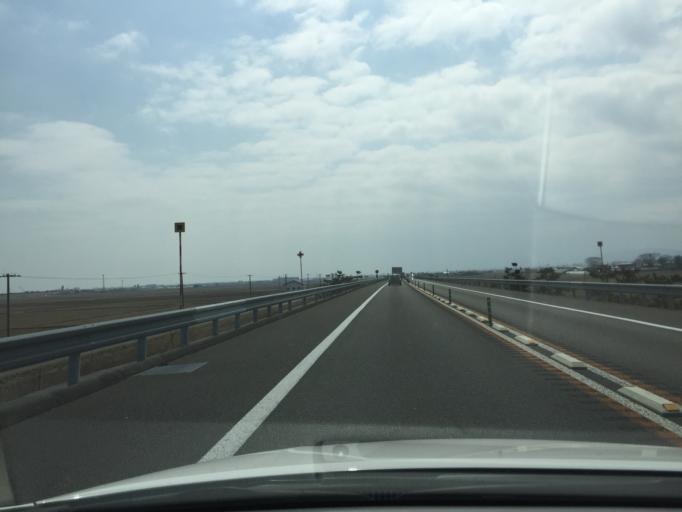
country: JP
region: Miyagi
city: Iwanuma
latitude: 38.0663
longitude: 140.8931
